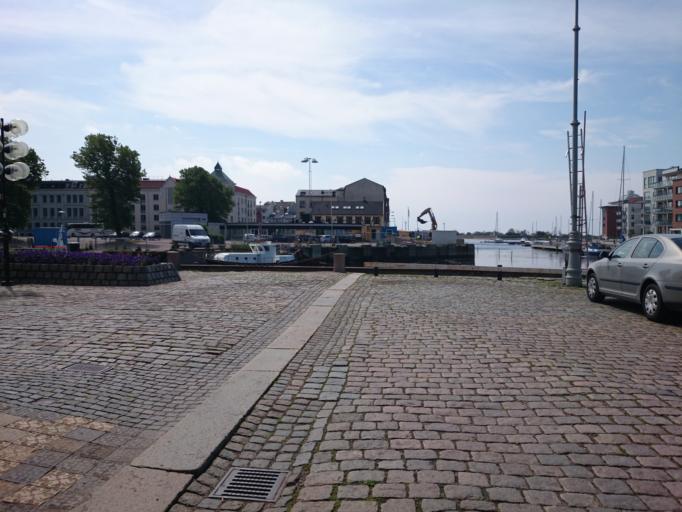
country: SE
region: Skane
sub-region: Landskrona
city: Landskrona
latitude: 55.8693
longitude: 12.8245
